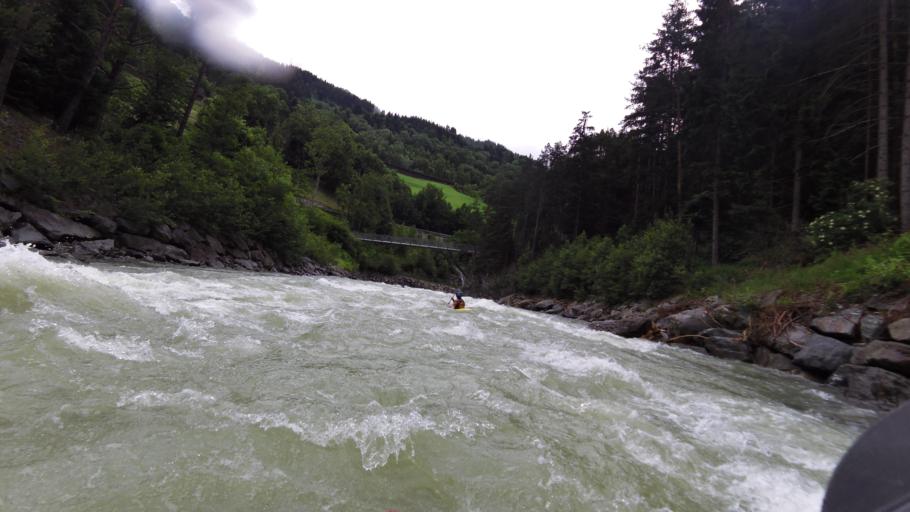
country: AT
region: Tyrol
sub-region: Politischer Bezirk Landeck
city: Pians
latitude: 47.1269
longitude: 10.4988
